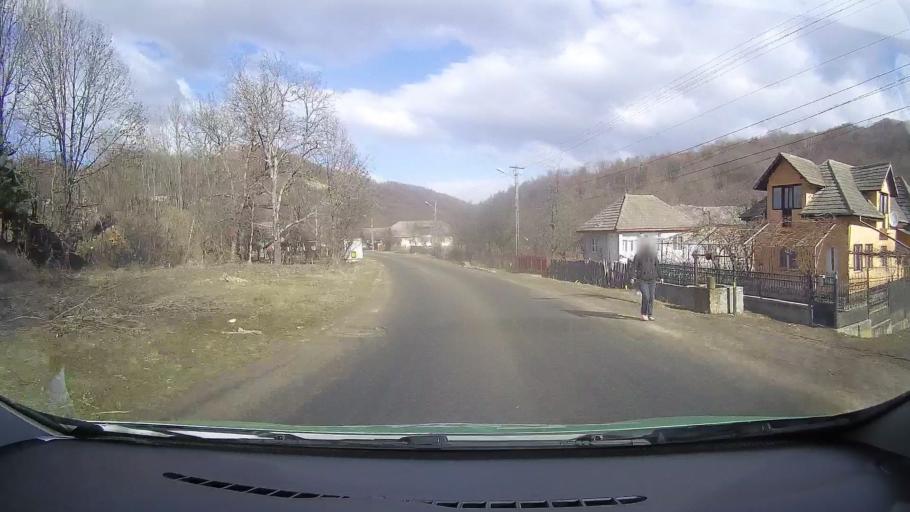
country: RO
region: Dambovita
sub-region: Oras Pucioasa
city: Pucioasa
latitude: 45.0982
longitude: 25.4438
